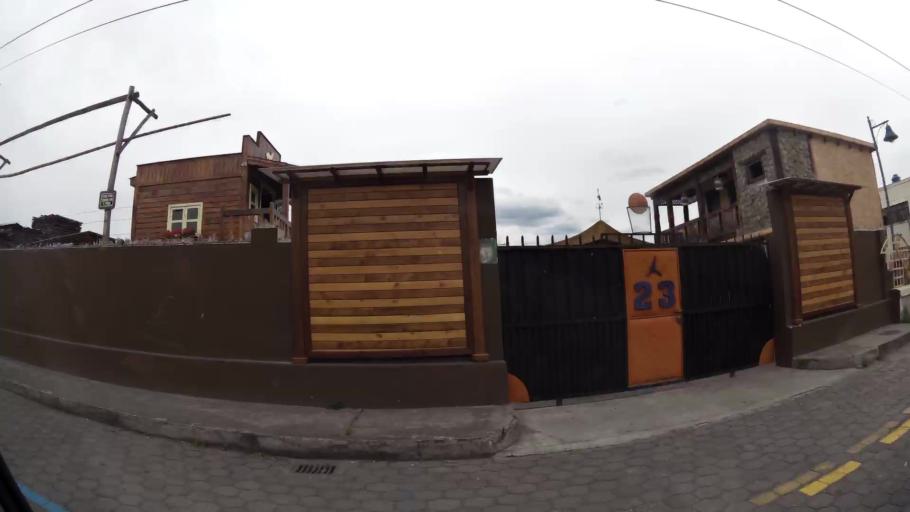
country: EC
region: Cotopaxi
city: Latacunga
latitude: -0.9392
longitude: -78.6132
